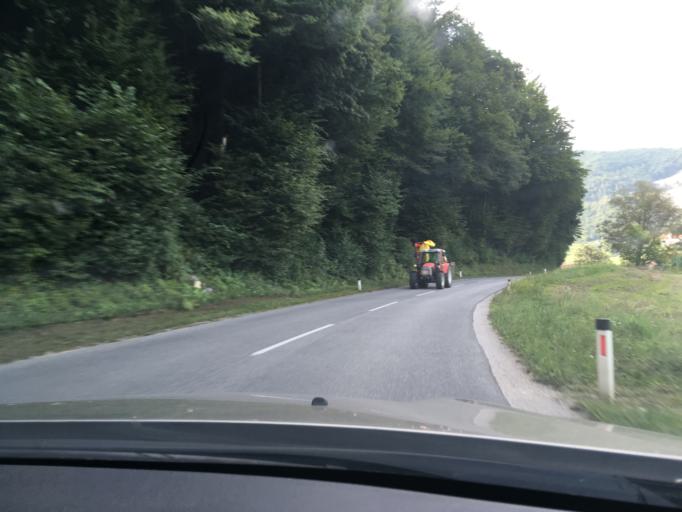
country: SI
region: Dolenjske Toplice
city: Dolenjske Toplice
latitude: 45.7712
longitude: 15.0228
